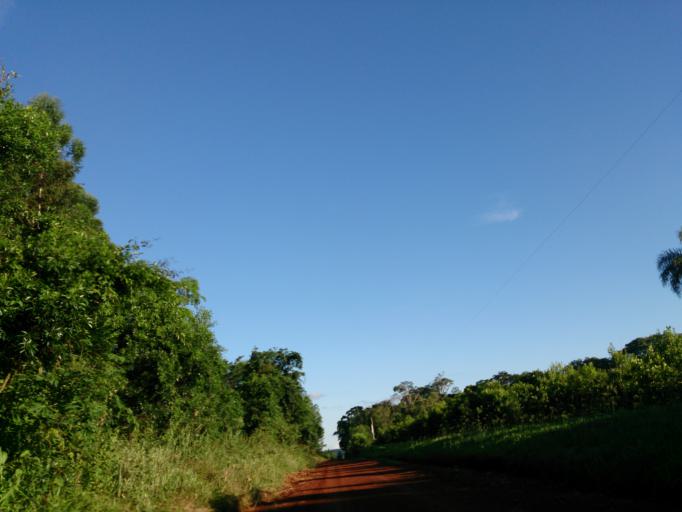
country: AR
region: Misiones
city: Florentino Ameghino
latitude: -27.5632
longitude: -55.1744
